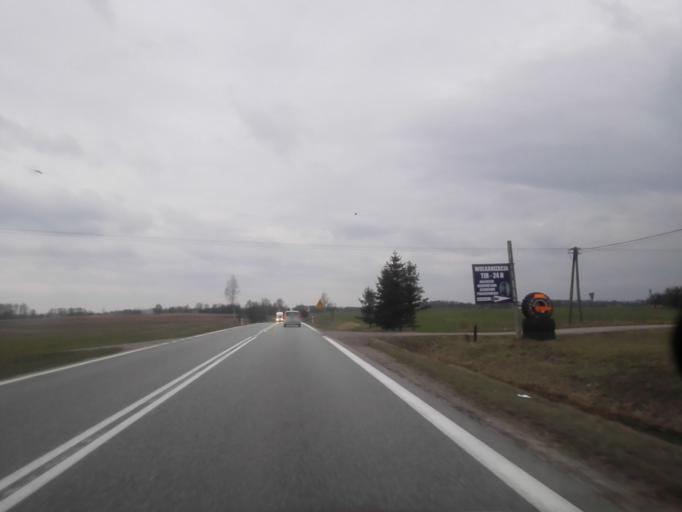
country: PL
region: Podlasie
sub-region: Powiat augustowski
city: Augustow
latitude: 53.8123
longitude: 22.9144
